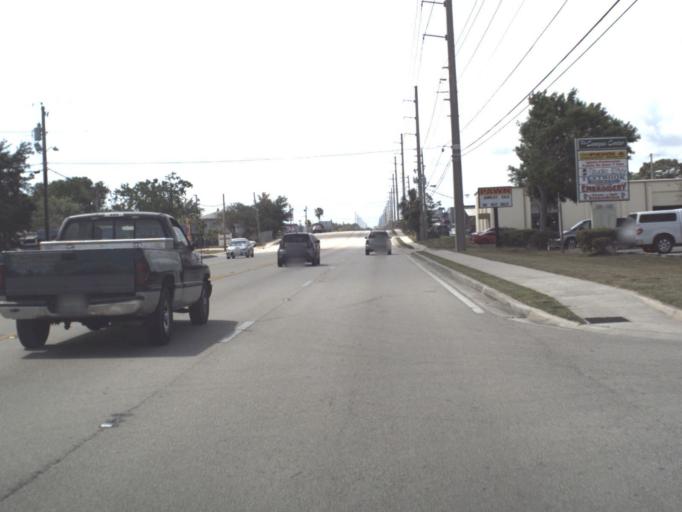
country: US
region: Florida
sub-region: Brevard County
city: Cocoa
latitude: 28.3797
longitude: -80.7551
